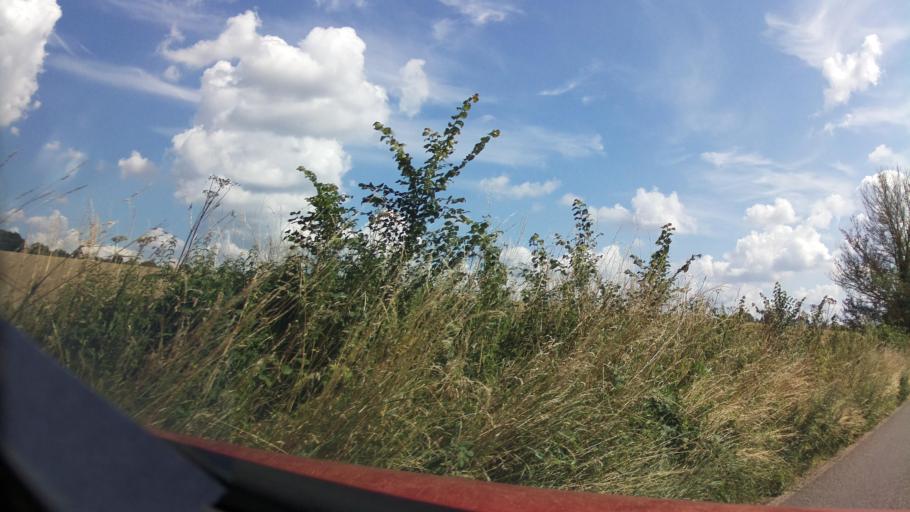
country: GB
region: England
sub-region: West Berkshire
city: Winterbourne
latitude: 51.4845
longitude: -1.3624
